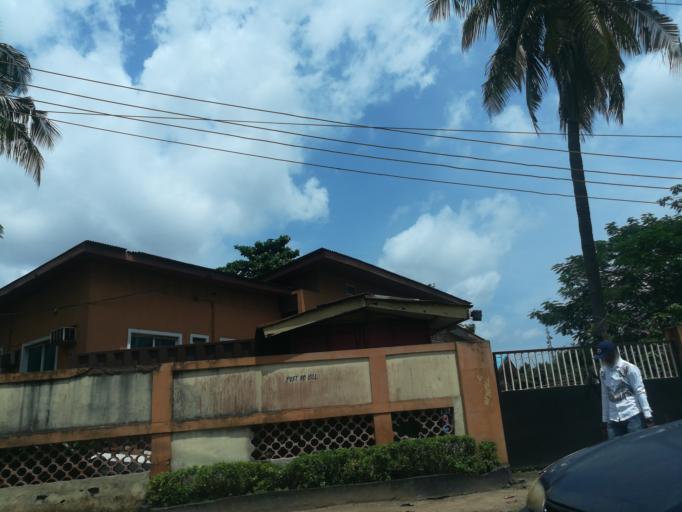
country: NG
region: Lagos
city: Somolu
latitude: 6.5423
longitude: 3.3626
